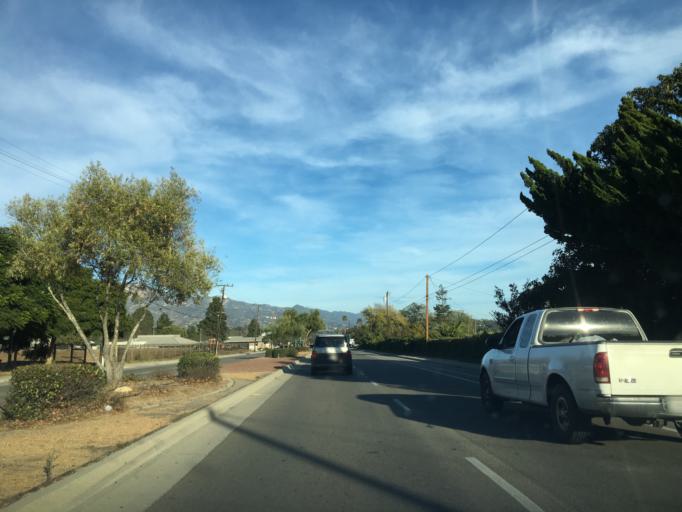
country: US
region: California
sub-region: Santa Barbara County
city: Goleta
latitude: 34.4357
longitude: -119.7941
